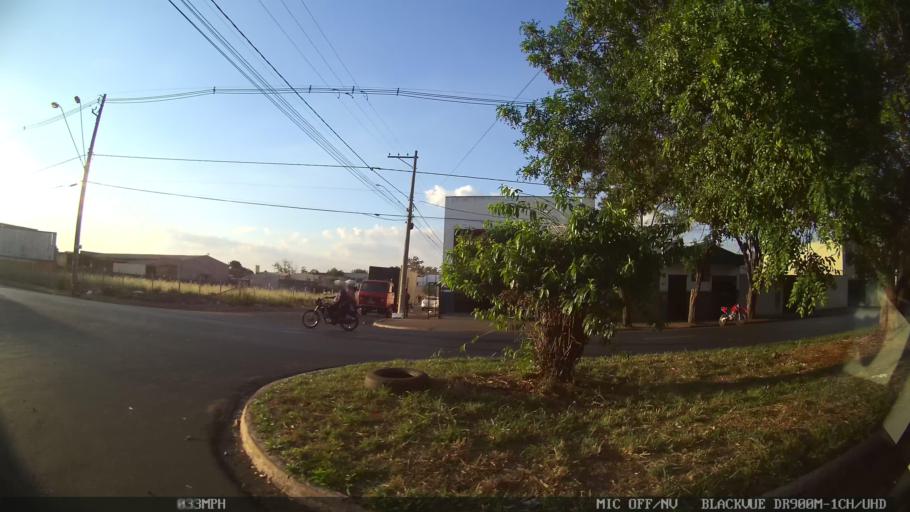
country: BR
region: Sao Paulo
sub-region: Ribeirao Preto
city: Ribeirao Preto
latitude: -21.1382
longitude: -47.7957
